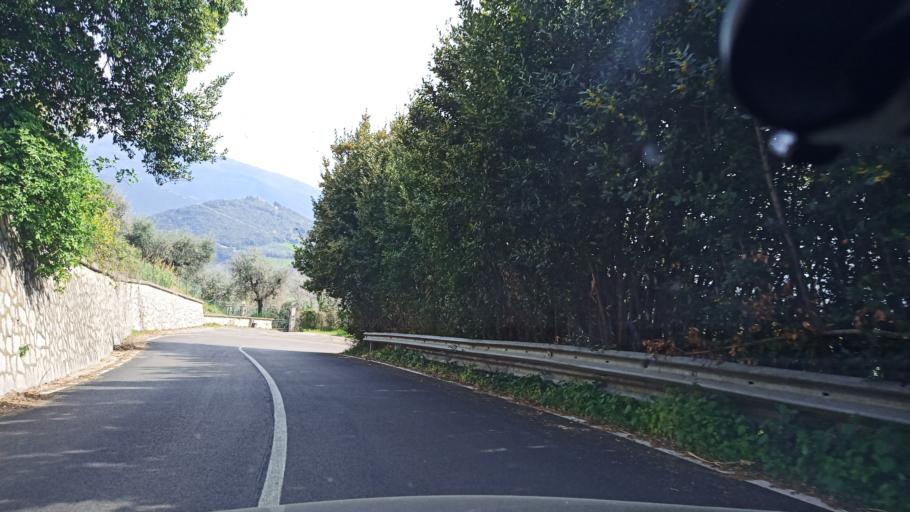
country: IT
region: Latium
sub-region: Provincia di Rieti
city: Torri in Sabina
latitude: 42.3326
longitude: 12.6453
